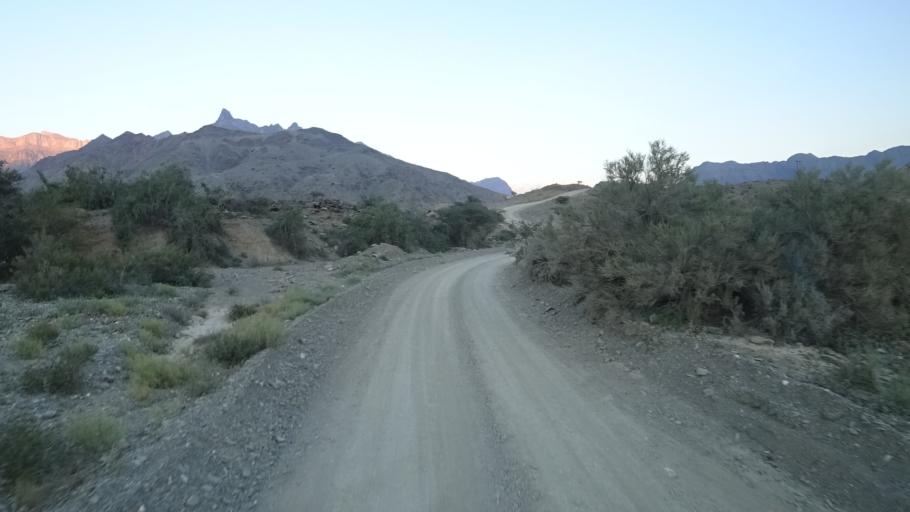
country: OM
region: Al Batinah
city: Rustaq
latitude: 23.2830
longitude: 57.3416
